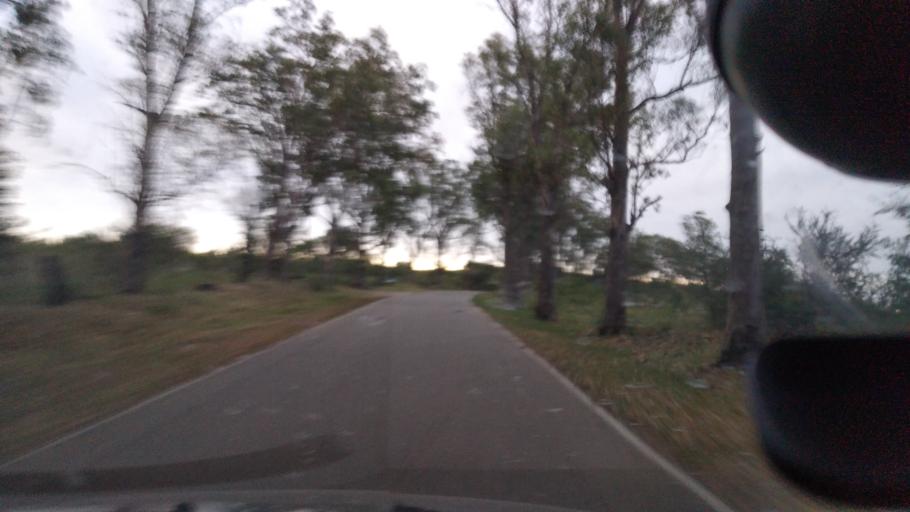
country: AR
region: Cordoba
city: Villa Las Rosas
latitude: -31.8783
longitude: -65.0273
